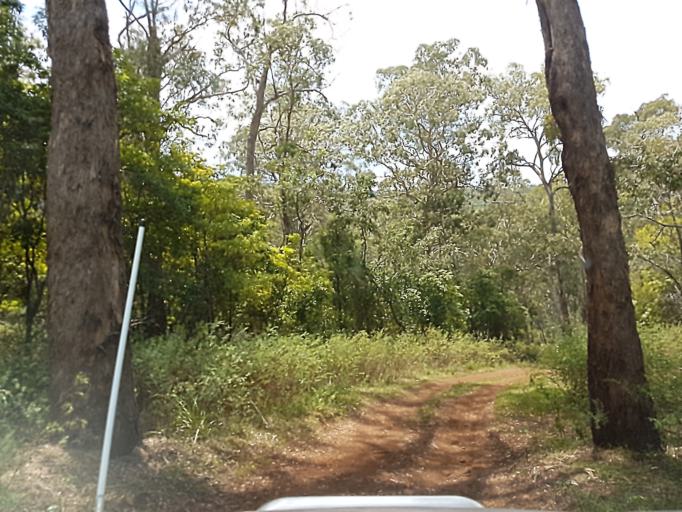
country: AU
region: Victoria
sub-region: East Gippsland
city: Lakes Entrance
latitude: -37.3570
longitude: 148.3566
